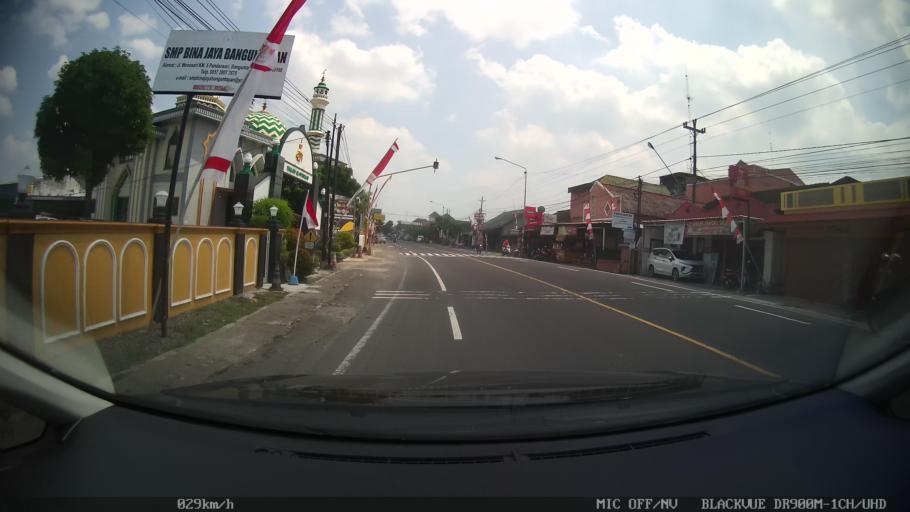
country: ID
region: Daerah Istimewa Yogyakarta
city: Depok
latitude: -7.8109
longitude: 110.4074
